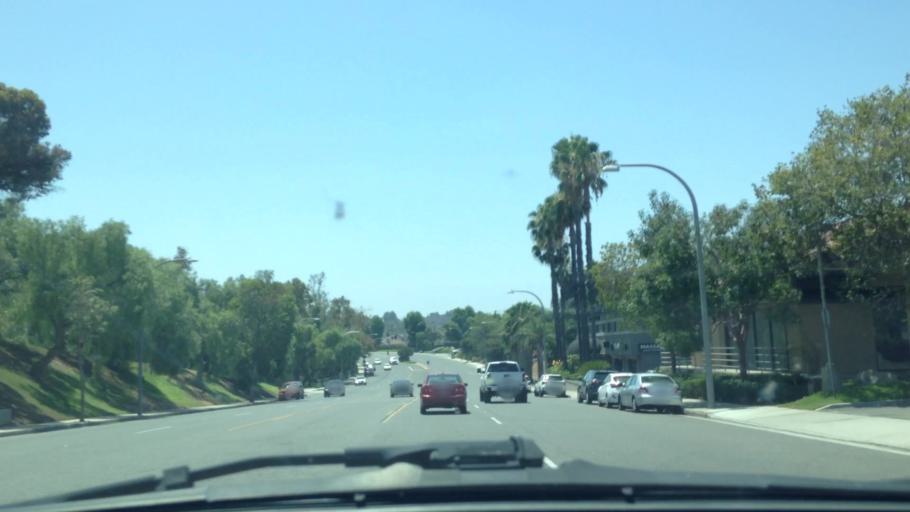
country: US
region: California
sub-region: Orange County
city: Brea
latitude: 33.9110
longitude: -117.8885
